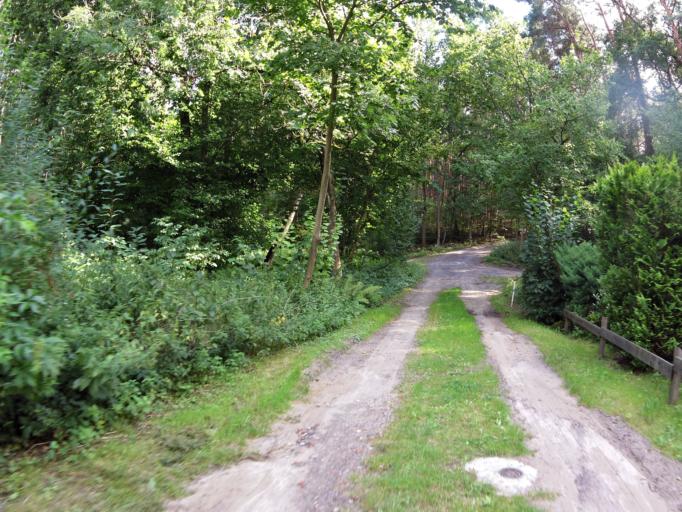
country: DE
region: Brandenburg
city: Munchehofe
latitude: 52.1857
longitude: 13.8953
